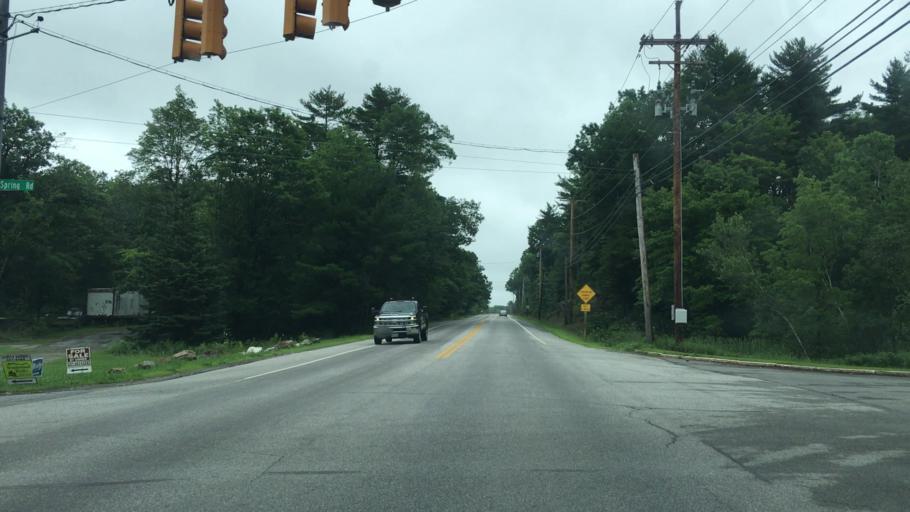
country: US
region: Maine
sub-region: Kennebec County
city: Chelsea
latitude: 44.2872
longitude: -69.7004
